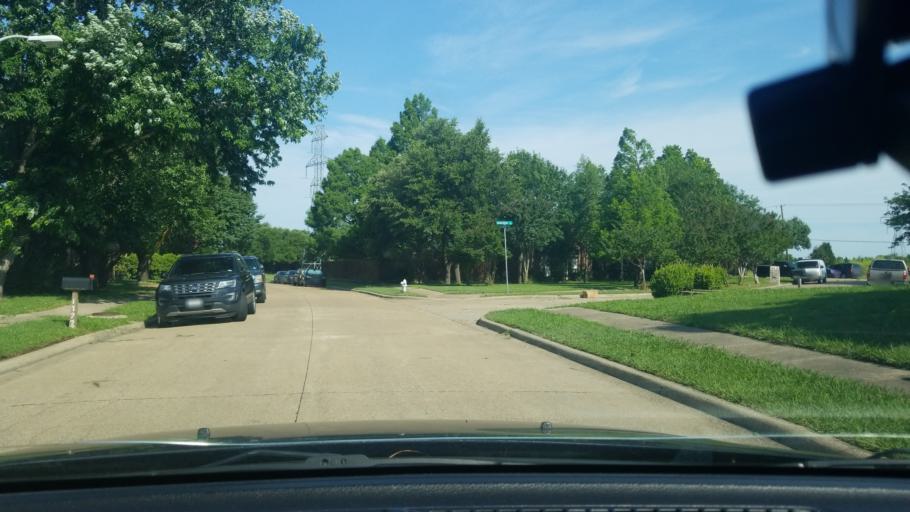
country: US
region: Texas
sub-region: Dallas County
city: Sunnyvale
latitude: 32.7790
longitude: -96.5717
